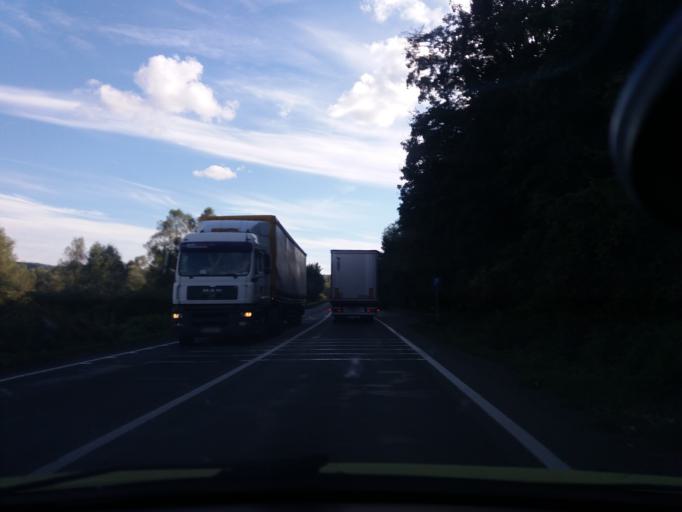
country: RO
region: Arad
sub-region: Comuna Barzava
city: Barzava
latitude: 46.1087
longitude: 21.9509
